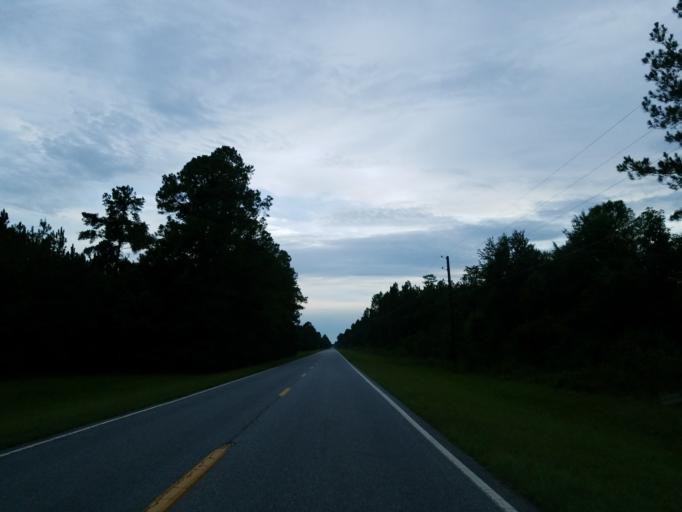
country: US
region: Georgia
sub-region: Echols County
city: Statenville
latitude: 30.7419
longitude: -83.0134
